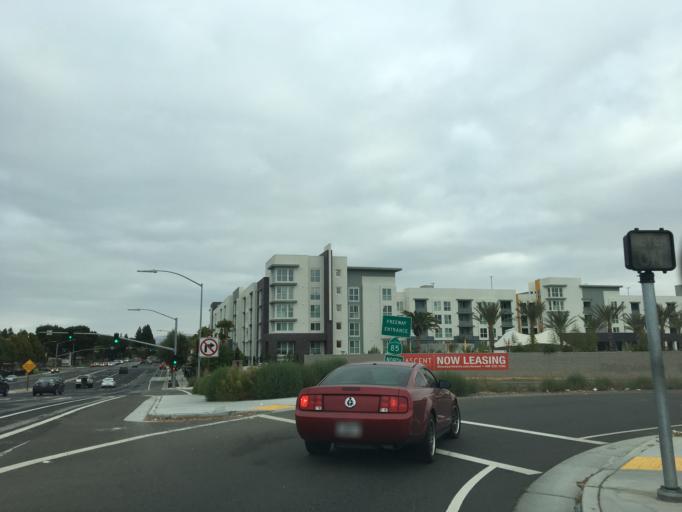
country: US
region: California
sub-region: Santa Clara County
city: Seven Trees
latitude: 37.2439
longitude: -121.8037
